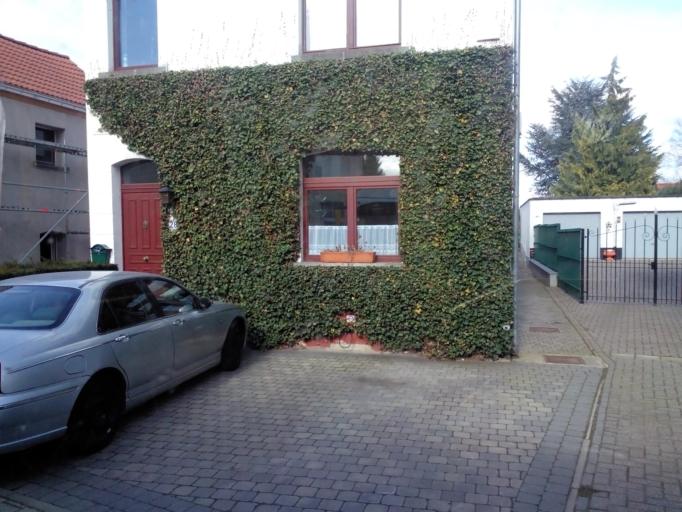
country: BE
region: Flanders
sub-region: Provincie Vlaams-Brabant
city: Wezembeek-Oppem
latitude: 50.8627
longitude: 4.5172
